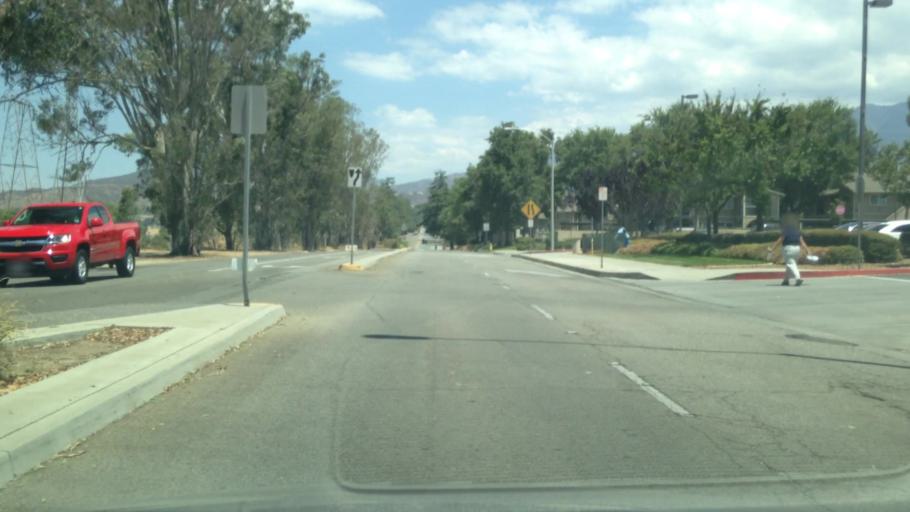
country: US
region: California
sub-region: Riverside County
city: Beaumont
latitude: 33.9480
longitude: -116.9772
